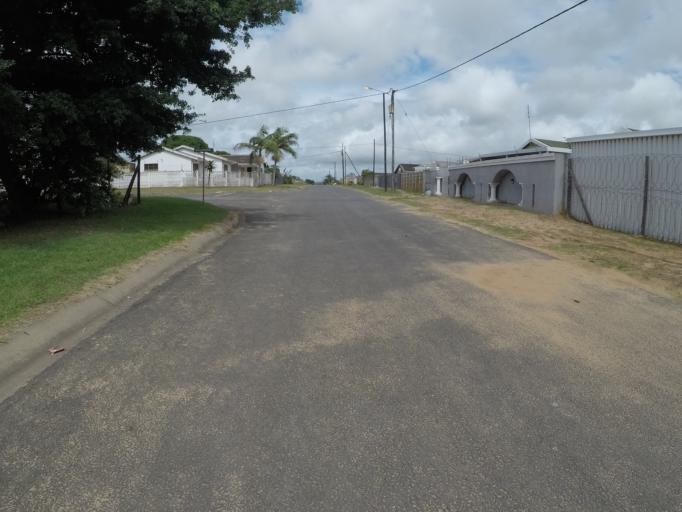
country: ZA
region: KwaZulu-Natal
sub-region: uThungulu District Municipality
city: eSikhawini
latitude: -28.8595
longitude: 31.9212
